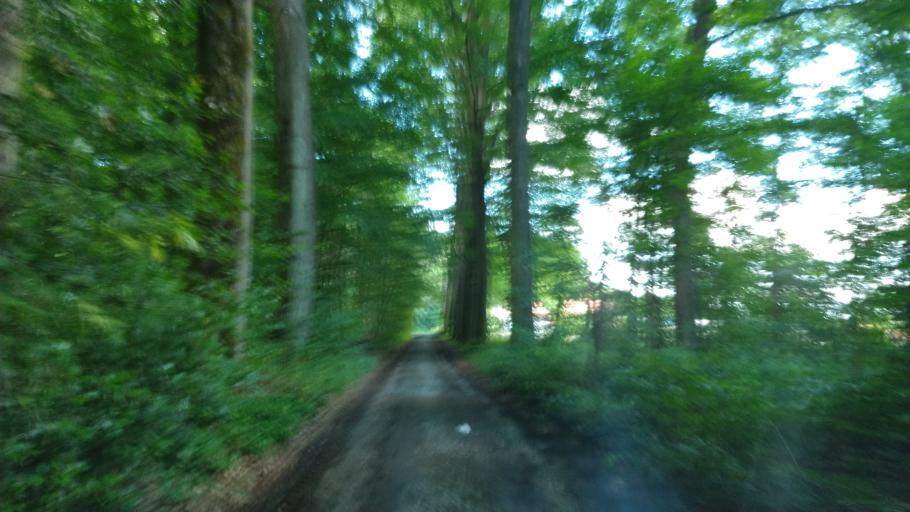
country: BE
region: Flanders
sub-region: Provincie Vlaams-Brabant
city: Bierbeek
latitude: 50.8130
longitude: 4.7474
